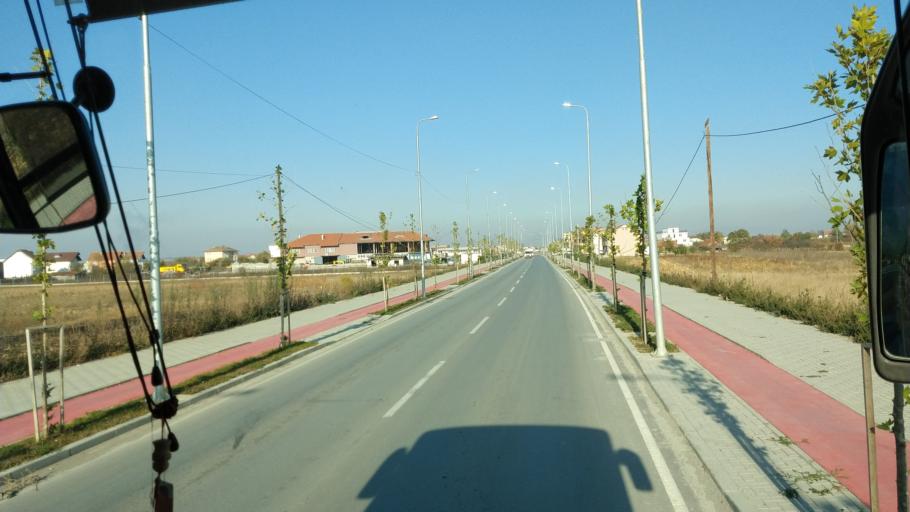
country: XK
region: Ferizaj
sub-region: Komuna e Shtimes
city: Shtime
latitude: 42.4431
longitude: 21.0553
